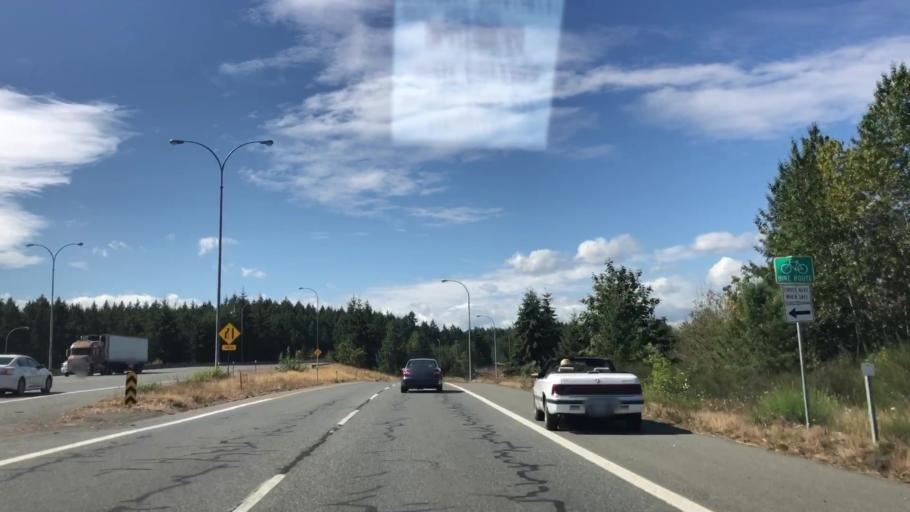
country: CA
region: British Columbia
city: Nanaimo
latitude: 49.1113
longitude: -123.8985
